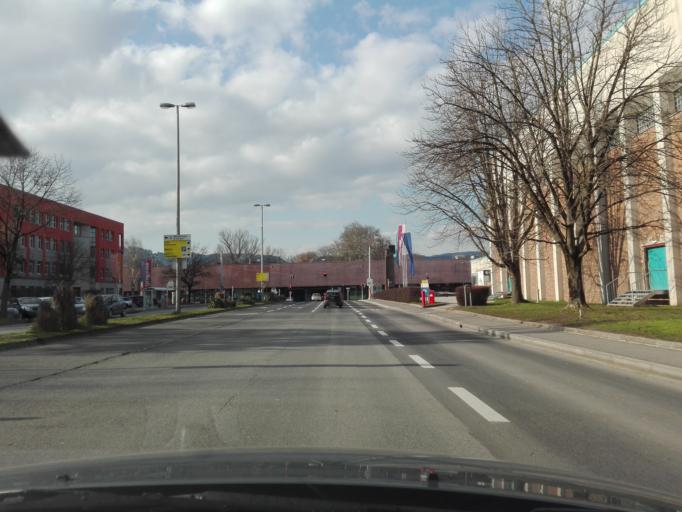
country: AT
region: Upper Austria
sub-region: Linz Stadt
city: Linz
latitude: 48.3109
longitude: 14.2977
